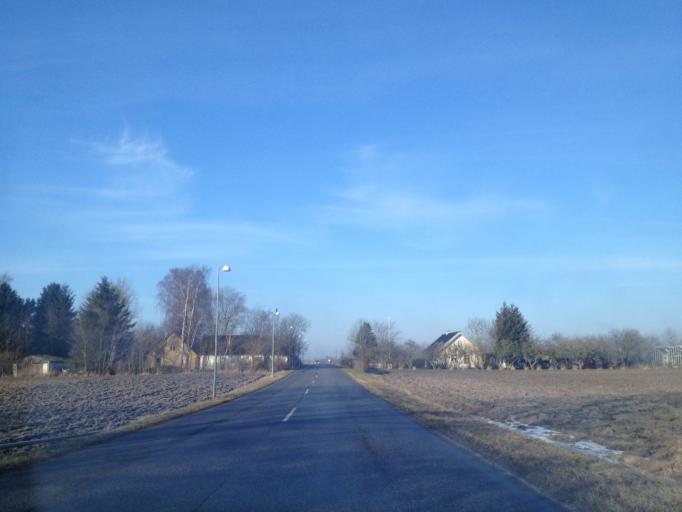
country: DK
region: Zealand
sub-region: Greve Kommune
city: Greve
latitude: 55.6079
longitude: 12.2838
